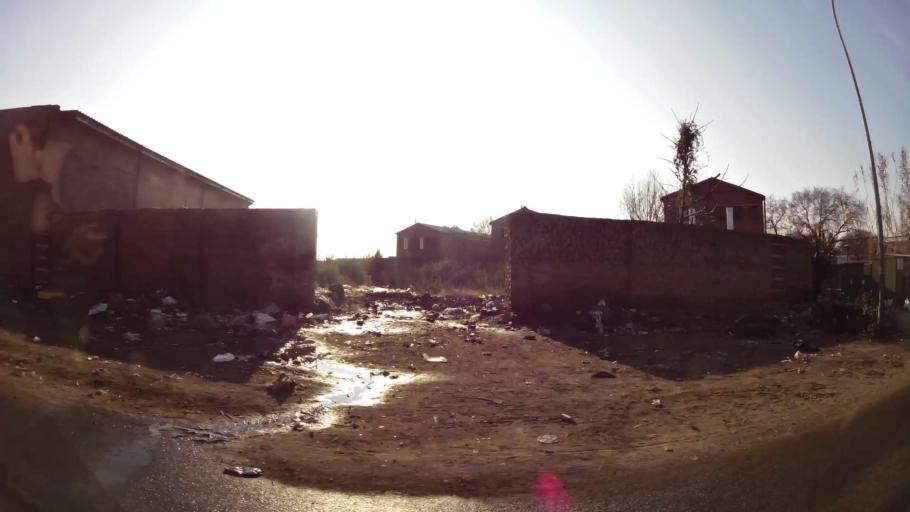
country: ZA
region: Orange Free State
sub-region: Mangaung Metropolitan Municipality
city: Bloemfontein
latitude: -29.1320
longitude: 26.2385
